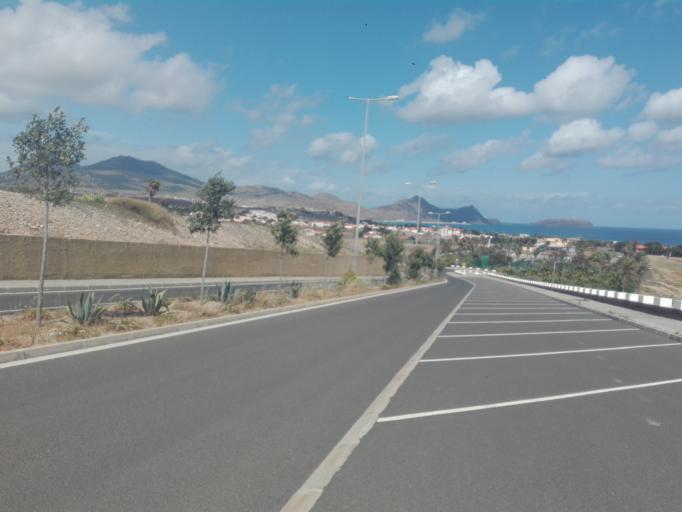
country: PT
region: Madeira
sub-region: Porto Santo
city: Vila de Porto Santo
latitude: 33.0462
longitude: -16.3609
